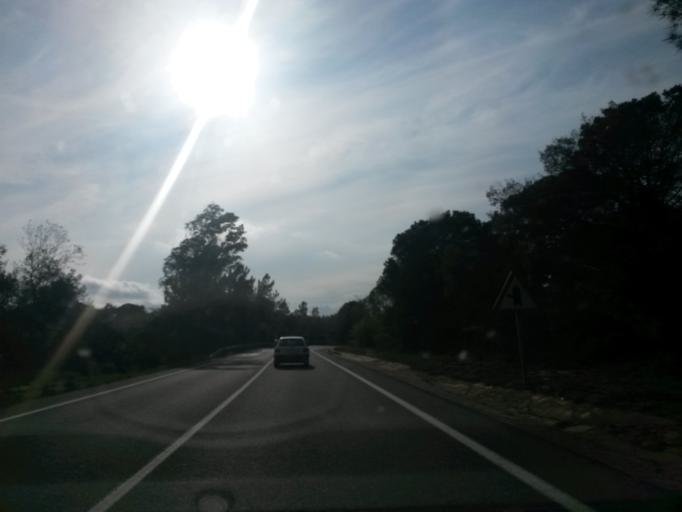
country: ES
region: Catalonia
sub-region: Provincia de Girona
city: Caldes de Malavella
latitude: 41.8444
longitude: 2.7828
